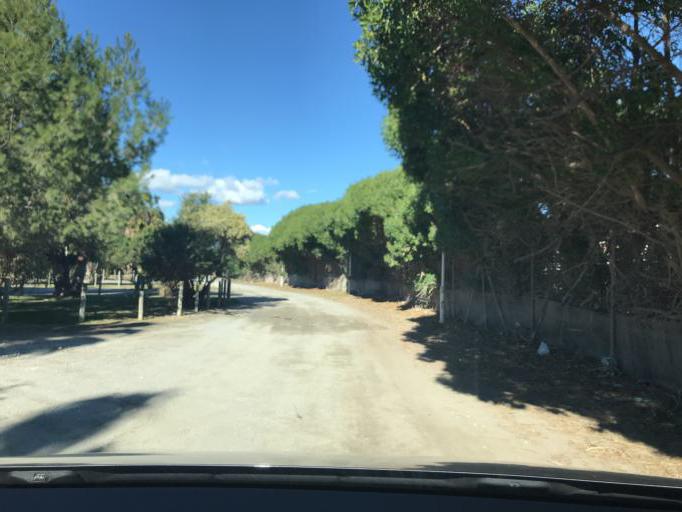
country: ES
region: Andalusia
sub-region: Provincia de Granada
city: Salobrena
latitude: 36.7178
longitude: -3.5591
